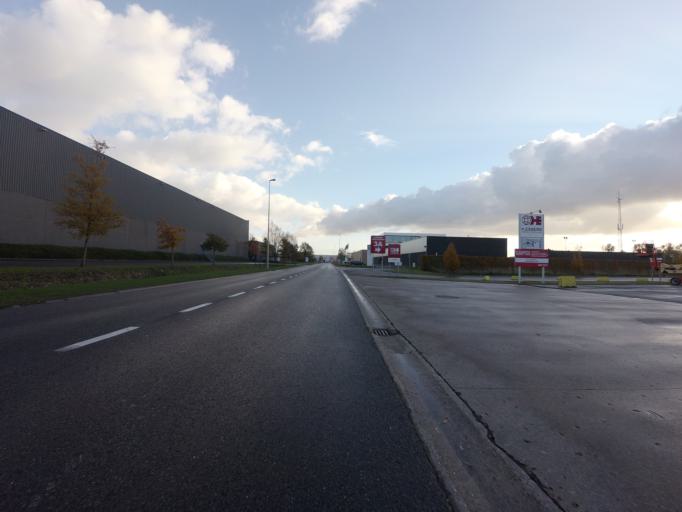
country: BE
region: Flanders
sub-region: Provincie Antwerpen
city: Boom
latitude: 51.0977
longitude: 4.3563
